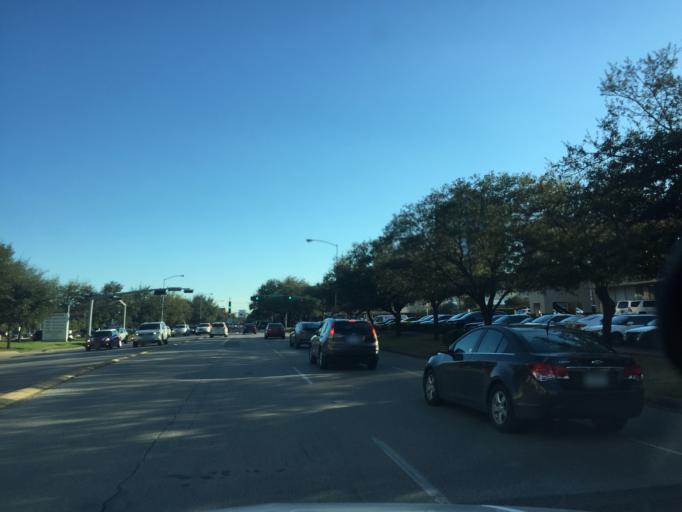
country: US
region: Texas
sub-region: Harris County
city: Houston
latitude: 29.7603
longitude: -95.3982
